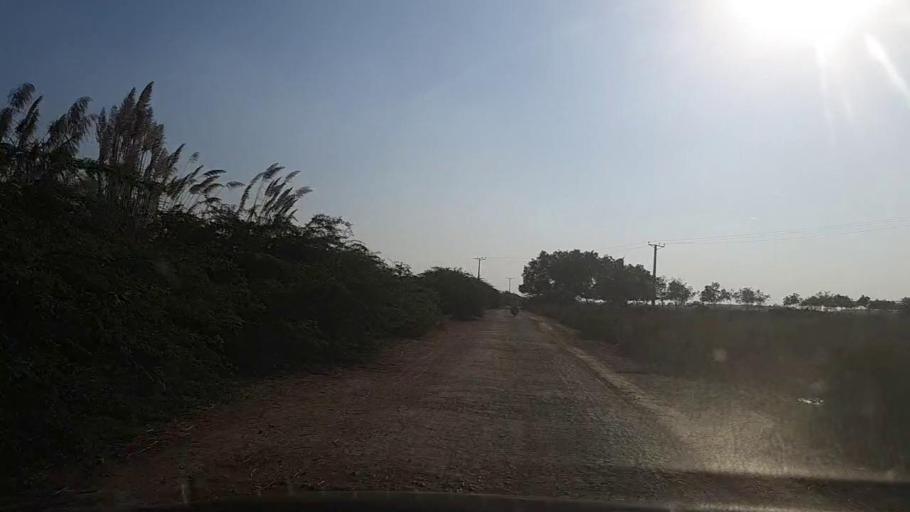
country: PK
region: Sindh
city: Gharo
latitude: 24.7136
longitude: 67.6858
